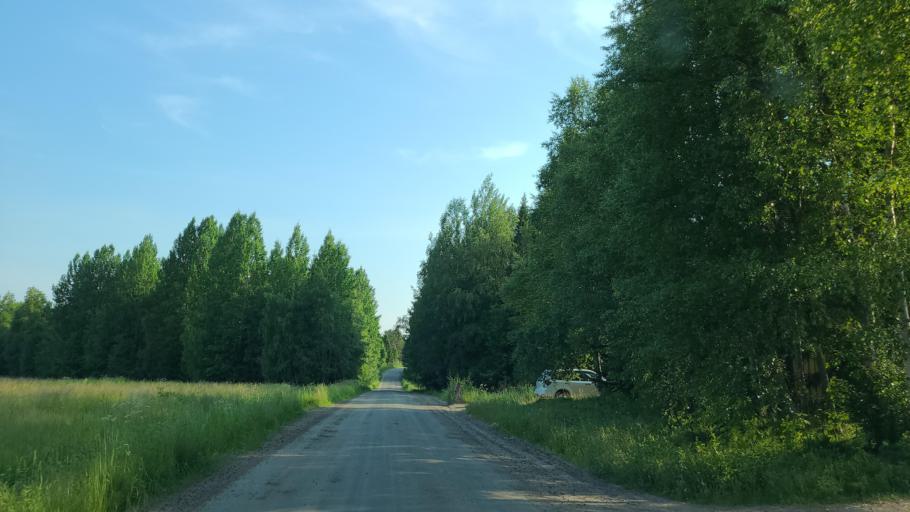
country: SE
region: Vaesterbotten
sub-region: Skelleftea Kommun
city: Burea
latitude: 64.4387
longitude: 21.5003
